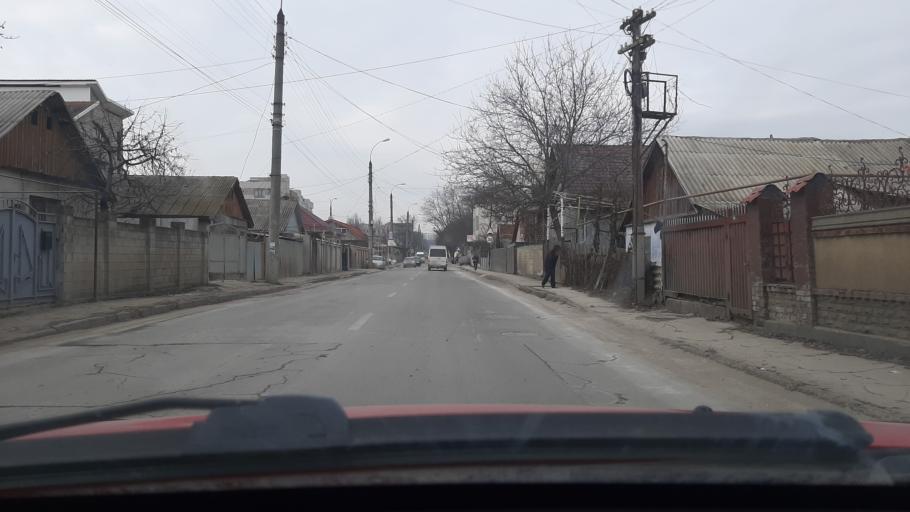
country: MD
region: Chisinau
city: Vatra
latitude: 47.0339
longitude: 28.7908
